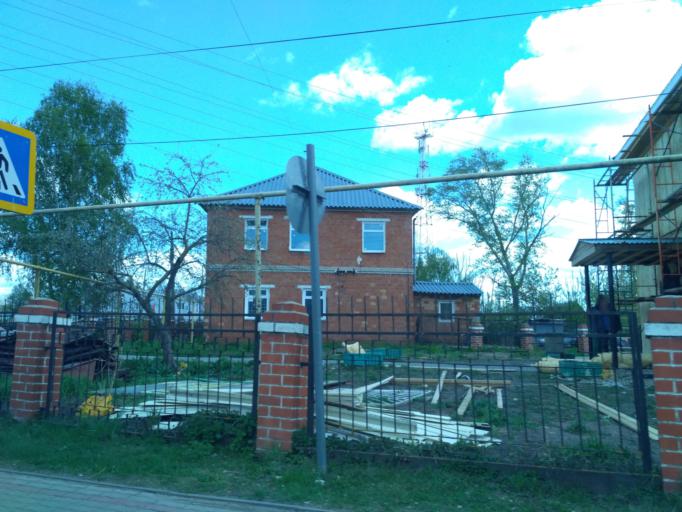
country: RU
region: Nizjnij Novgorod
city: Vad
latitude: 55.5331
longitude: 44.2142
